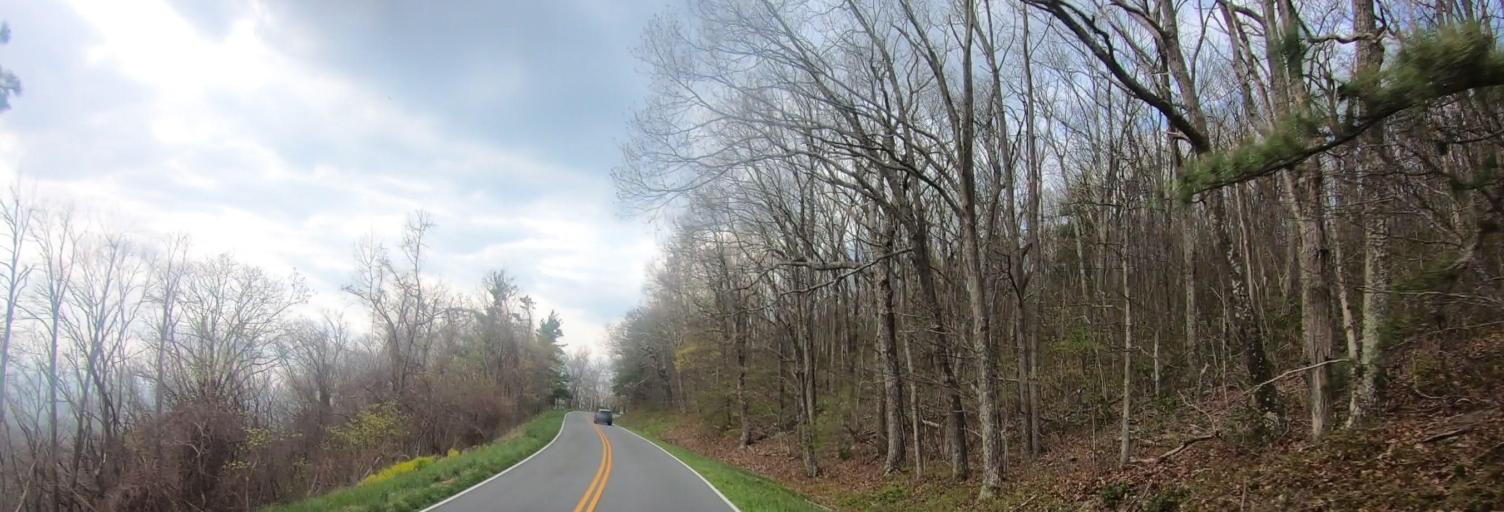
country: US
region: Virginia
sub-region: Augusta County
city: Crimora
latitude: 38.1371
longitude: -78.7816
